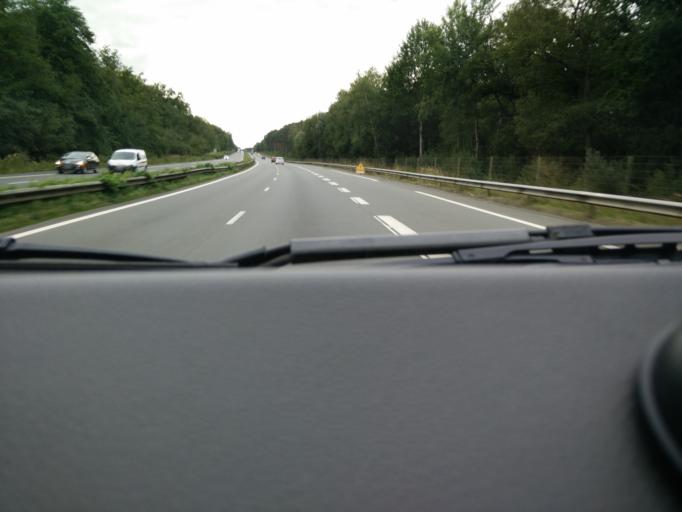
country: FR
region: Nord-Pas-de-Calais
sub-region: Departement du Nord
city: Saint-Amand-les-Eaux
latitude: 50.4087
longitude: 3.4381
